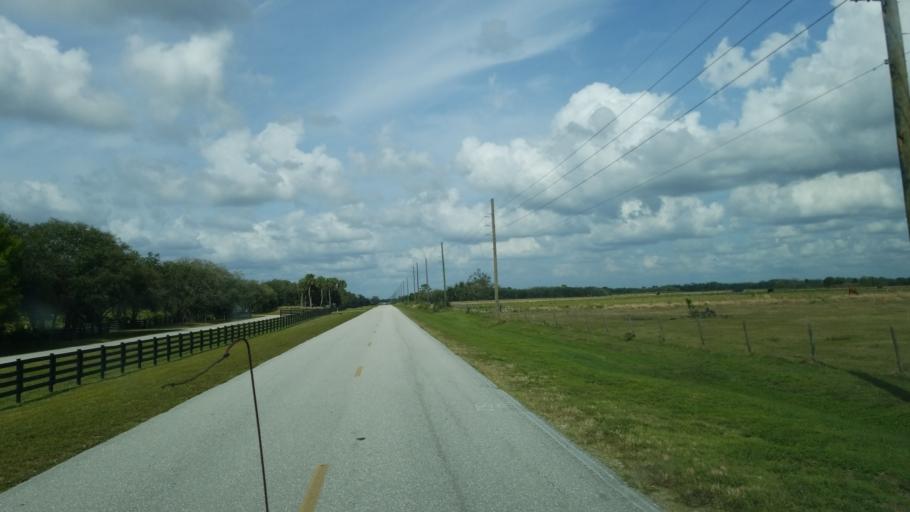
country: US
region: Florida
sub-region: Okeechobee County
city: Cypress Quarters
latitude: 27.4555
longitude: -80.7714
